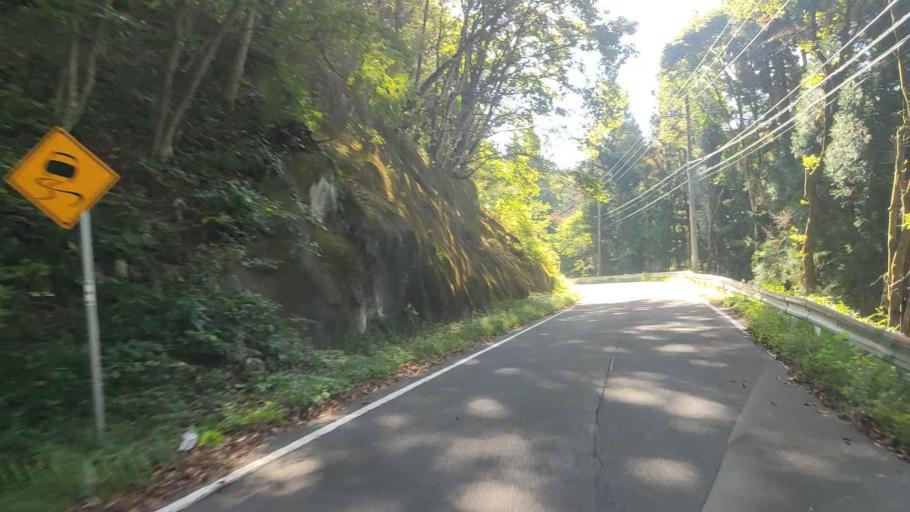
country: JP
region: Gunma
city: Nakanojomachi
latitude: 36.5996
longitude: 138.6431
